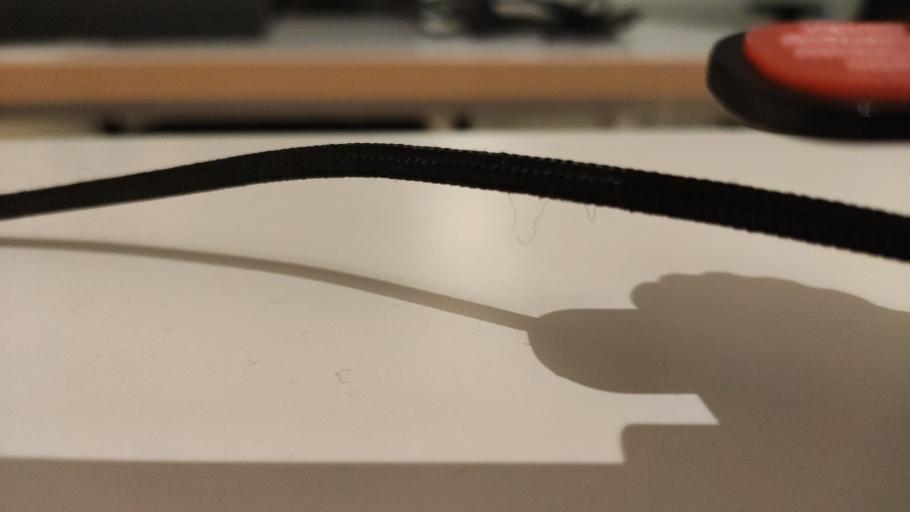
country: RU
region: Moskovskaya
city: Semkhoz
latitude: 56.3980
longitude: 38.0348
